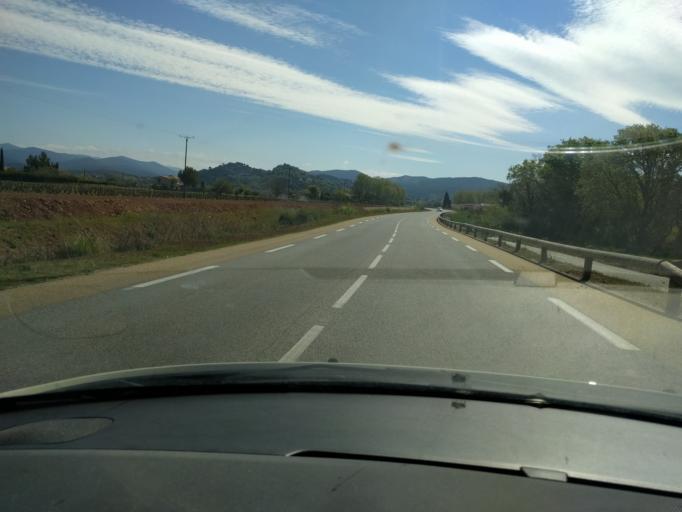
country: FR
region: Provence-Alpes-Cote d'Azur
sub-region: Departement du Var
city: Pierrefeu-du-Var
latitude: 43.2275
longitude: 6.1197
